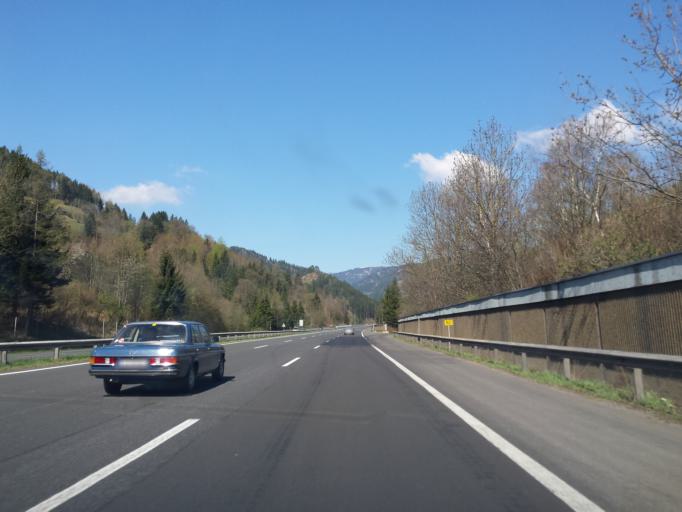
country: AT
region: Styria
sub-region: Politischer Bezirk Graz-Umgebung
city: Ubelbach
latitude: 47.2267
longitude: 15.2240
